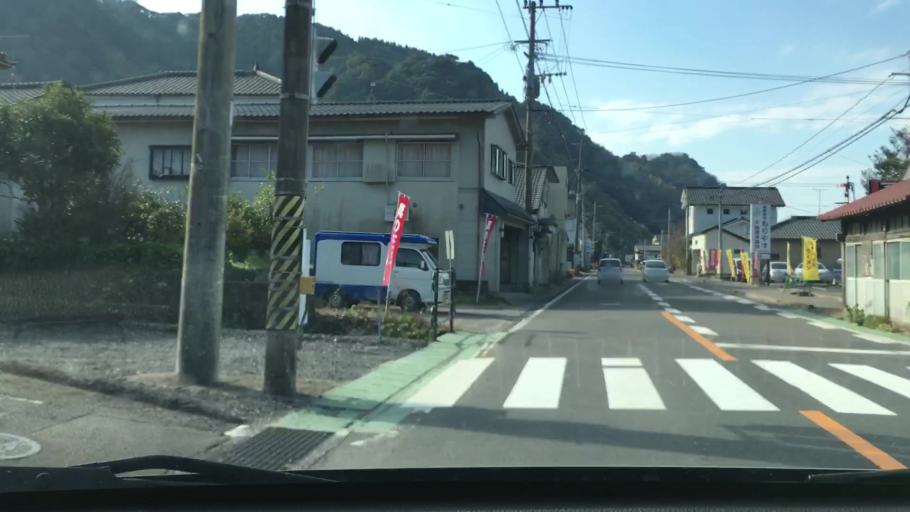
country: JP
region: Kagoshima
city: Hamanoichi
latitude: 31.6098
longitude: 130.7946
